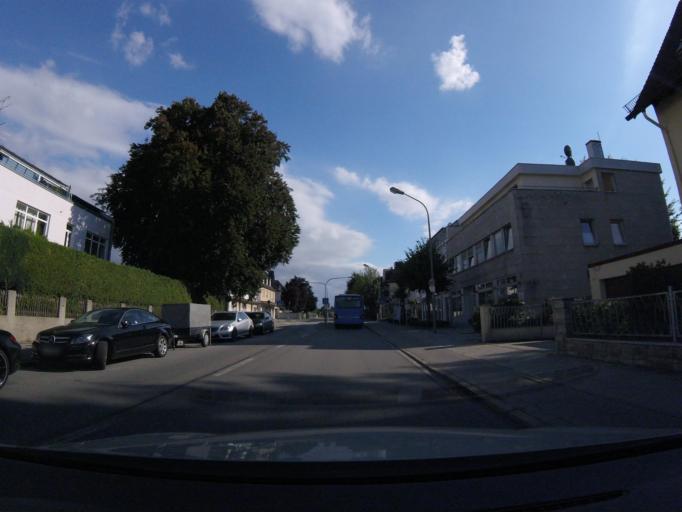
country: DE
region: Bavaria
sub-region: Upper Bavaria
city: Bogenhausen
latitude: 48.1524
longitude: 11.6410
